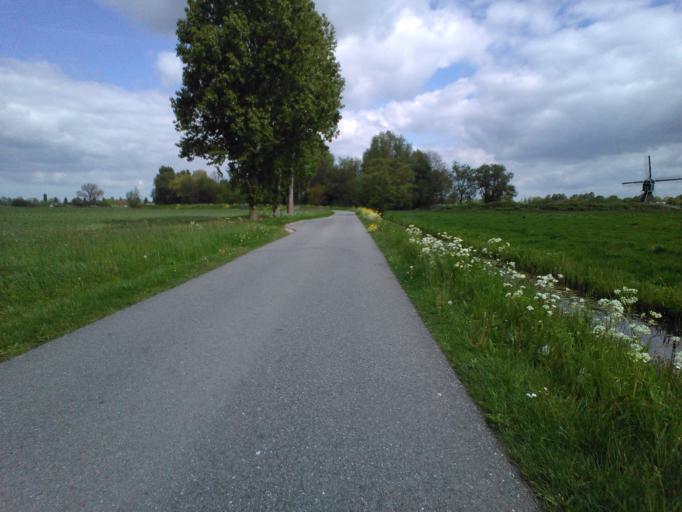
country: NL
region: South Holland
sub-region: Bodegraven-Reeuwijk
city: Bodegraven
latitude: 52.0773
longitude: 4.7927
